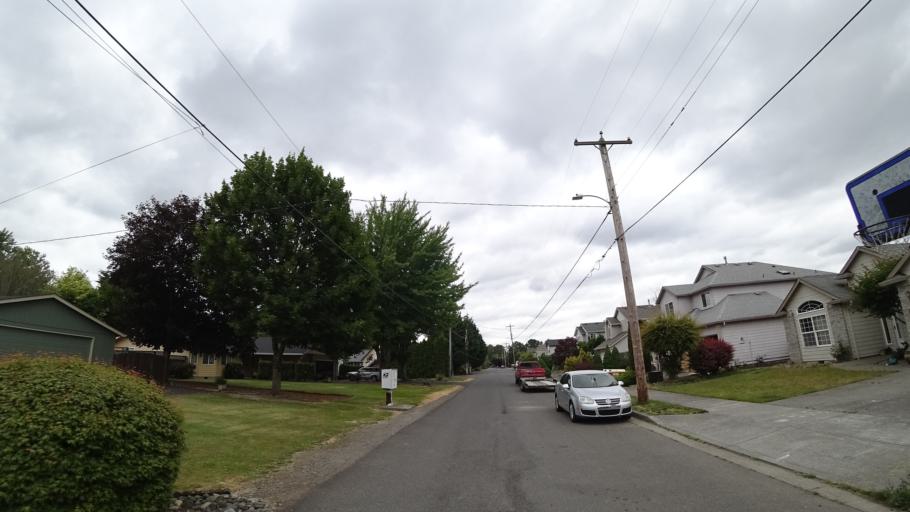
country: US
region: Washington
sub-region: Clark County
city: Vancouver
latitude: 45.5892
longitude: -122.6453
